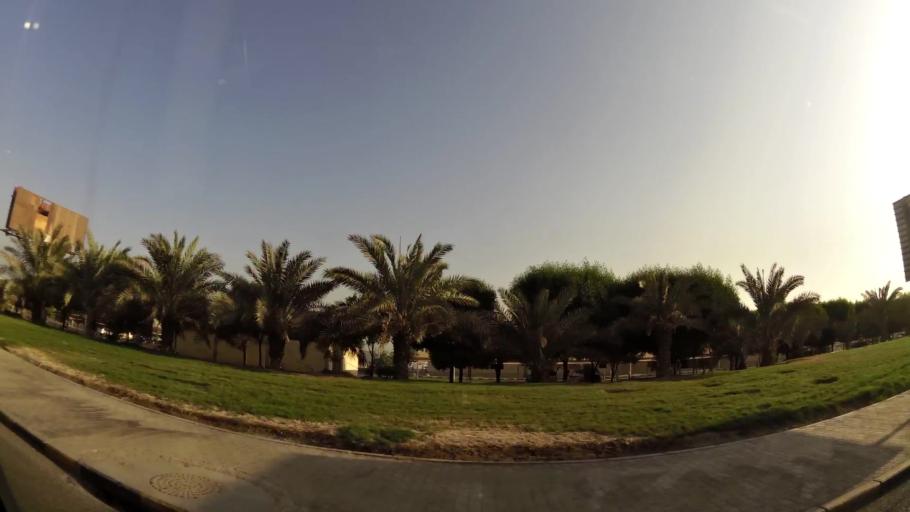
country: KW
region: Muhafazat Hawalli
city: Hawalli
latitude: 29.3406
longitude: 48.0513
